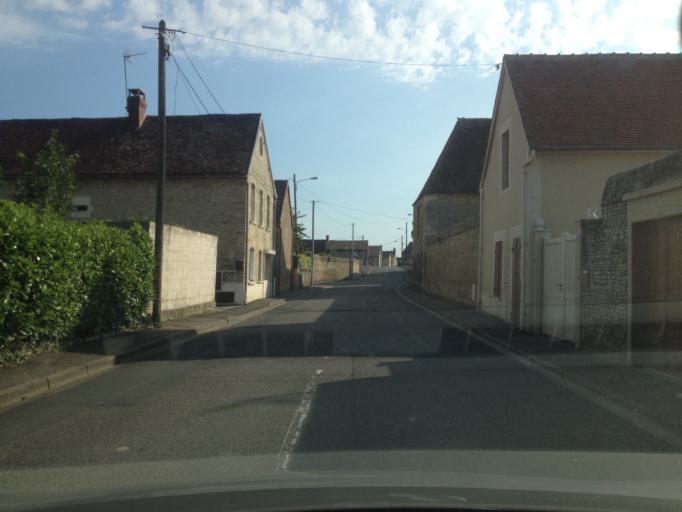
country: FR
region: Lower Normandy
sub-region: Departement du Calvados
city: Canon
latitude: 49.0750
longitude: -0.0949
